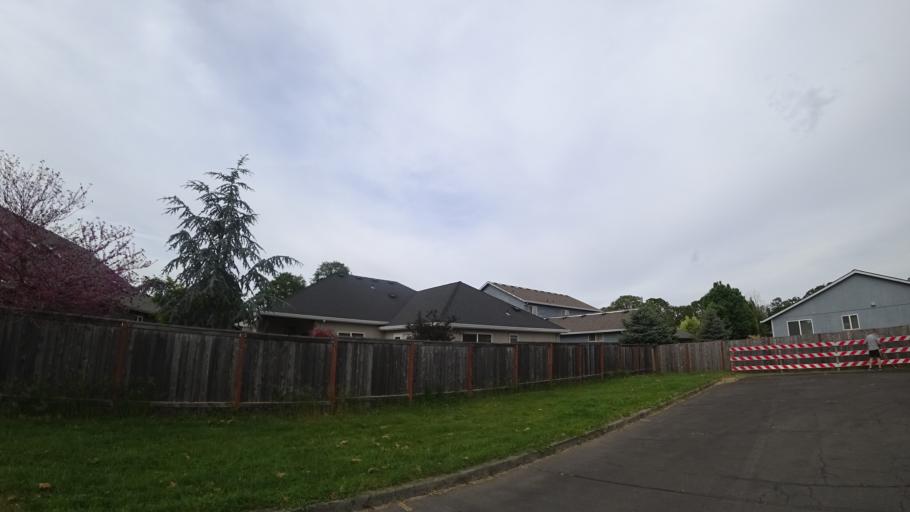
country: US
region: Oregon
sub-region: Washington County
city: Aloha
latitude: 45.5051
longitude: -122.9240
